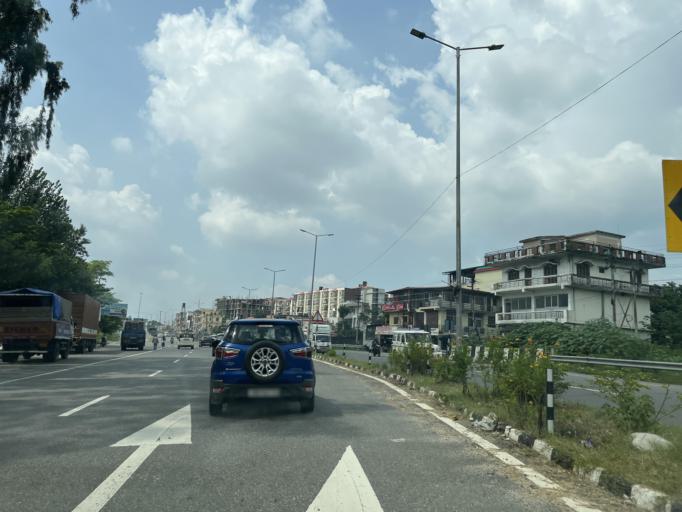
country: IN
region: Uttarakhand
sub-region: Dehradun
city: Raipur
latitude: 30.2698
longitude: 78.0802
